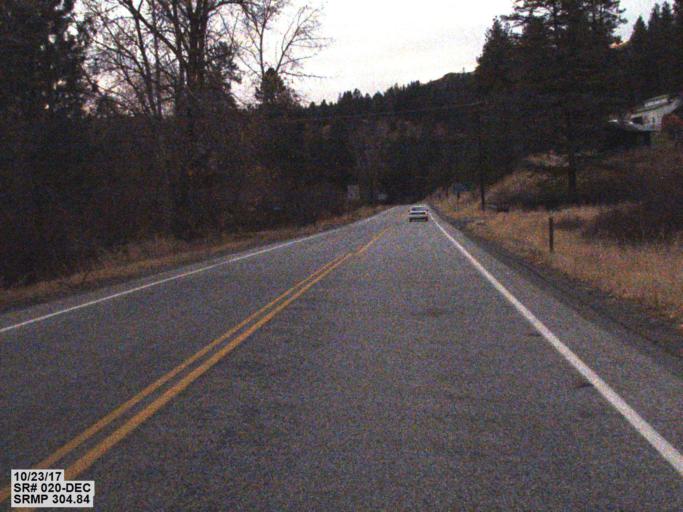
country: US
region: Washington
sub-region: Ferry County
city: Republic
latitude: 48.6517
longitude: -118.6928
